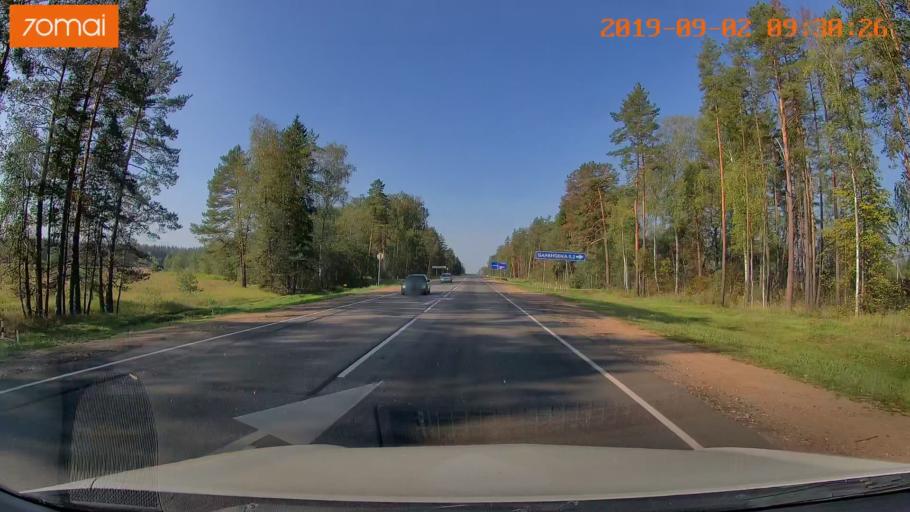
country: RU
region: Kaluga
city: Yukhnov
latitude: 54.7337
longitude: 35.1967
